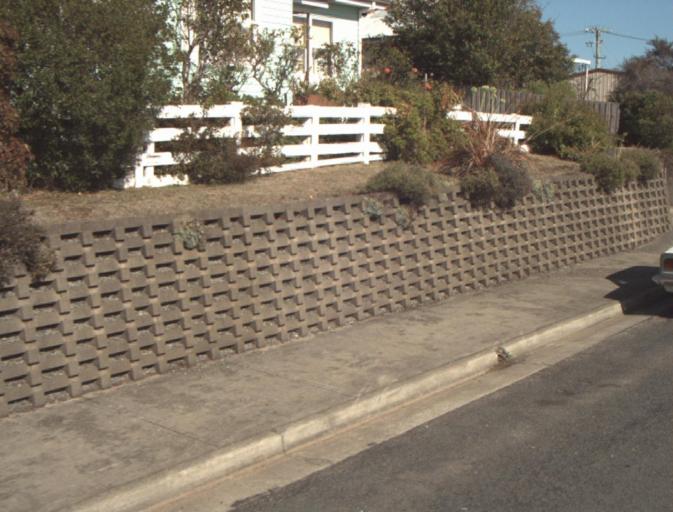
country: AU
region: Tasmania
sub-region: Launceston
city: Mayfield
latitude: -41.3694
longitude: 147.1403
